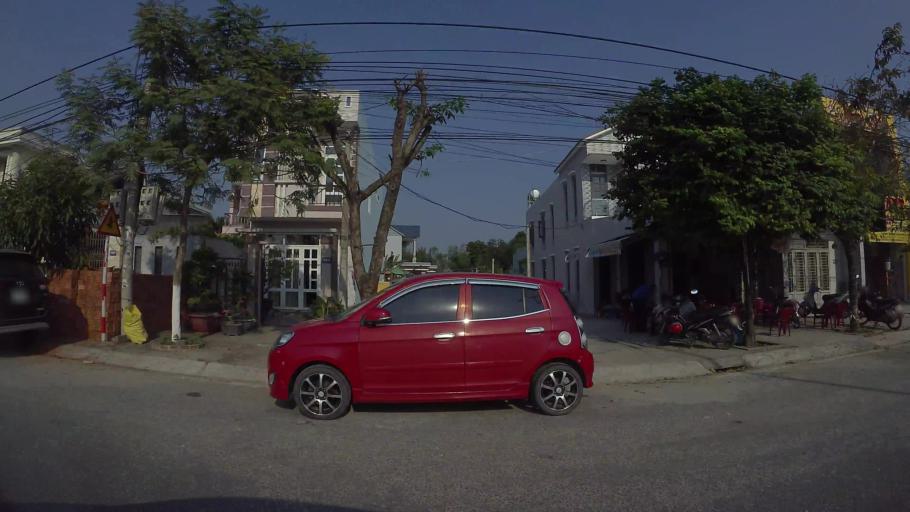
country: VN
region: Quang Nam
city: Quang Nam
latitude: 15.9479
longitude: 108.2547
